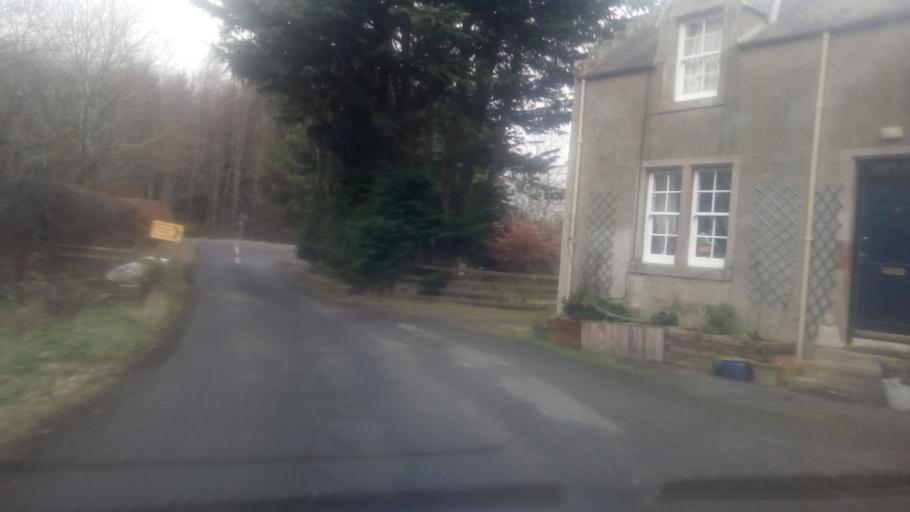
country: GB
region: Scotland
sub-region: The Scottish Borders
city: Kelso
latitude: 55.5739
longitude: -2.5176
